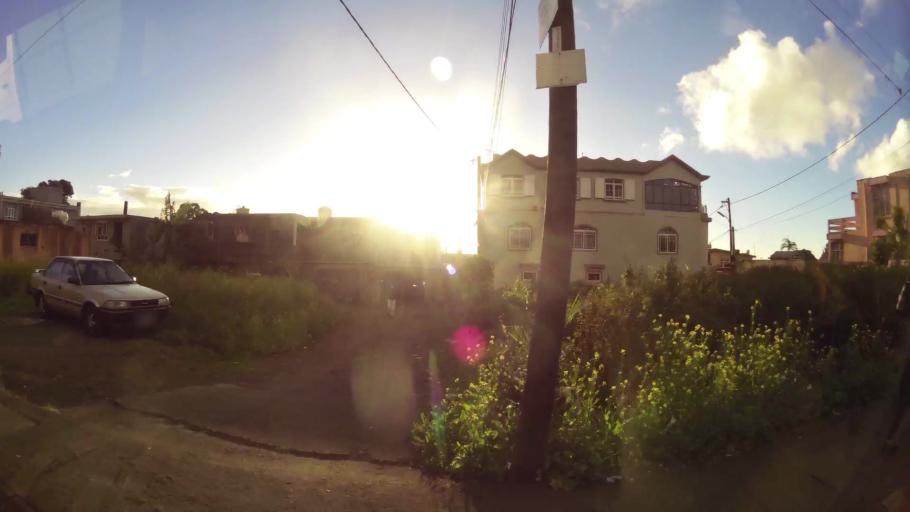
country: MU
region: Plaines Wilhems
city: Curepipe
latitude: -20.3063
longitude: 57.5300
